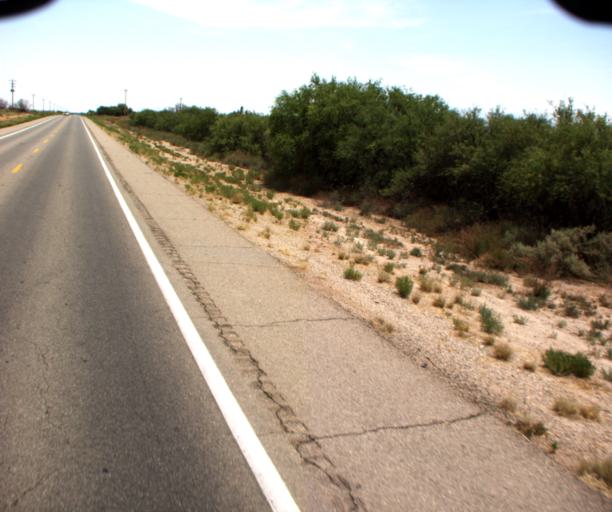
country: US
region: Arizona
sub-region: Graham County
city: Bylas
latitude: 33.0549
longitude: -109.9965
